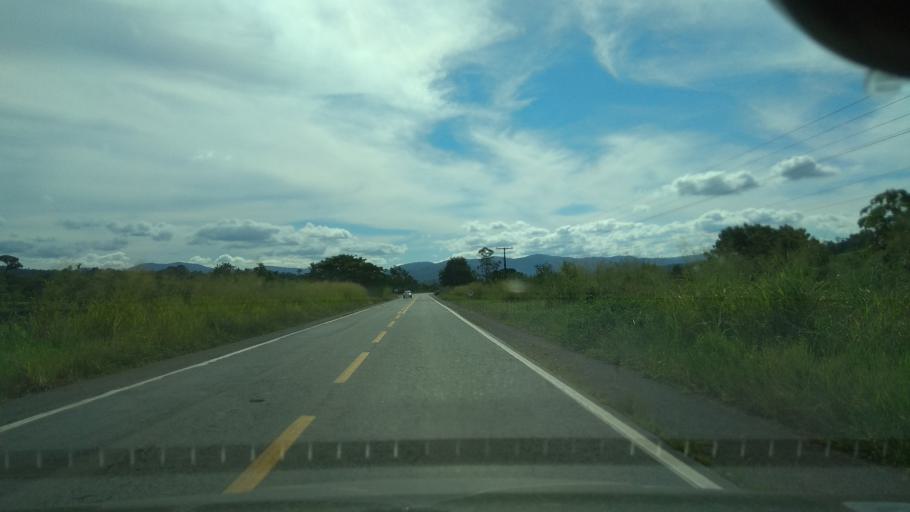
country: BR
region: Bahia
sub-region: Jitauna
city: Jitauna
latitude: -14.0383
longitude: -39.8267
